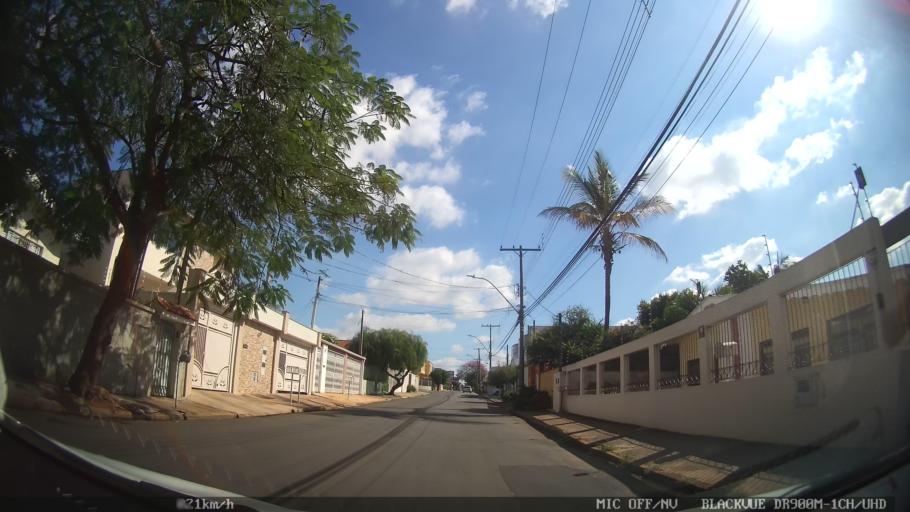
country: BR
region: Sao Paulo
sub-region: Hortolandia
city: Hortolandia
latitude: -22.8721
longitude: -47.2245
